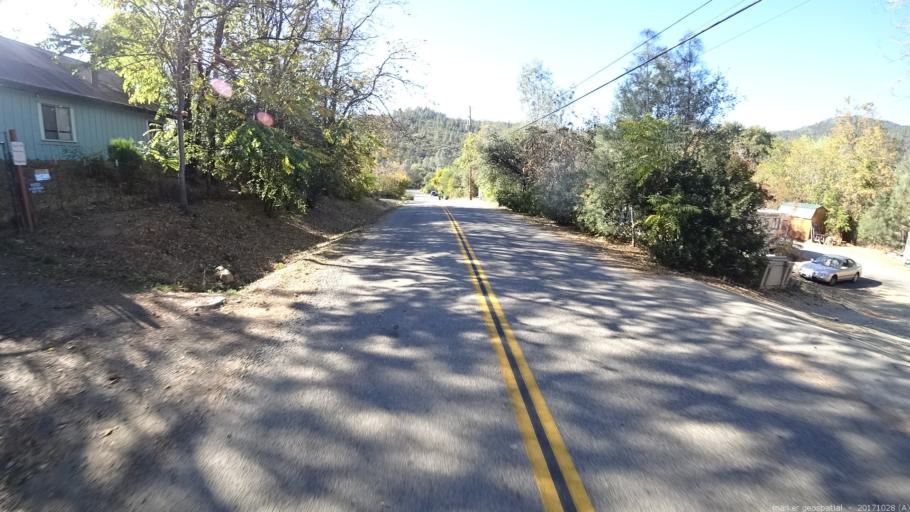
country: US
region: California
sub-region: Shasta County
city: Shasta
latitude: 40.6226
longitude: -122.4642
